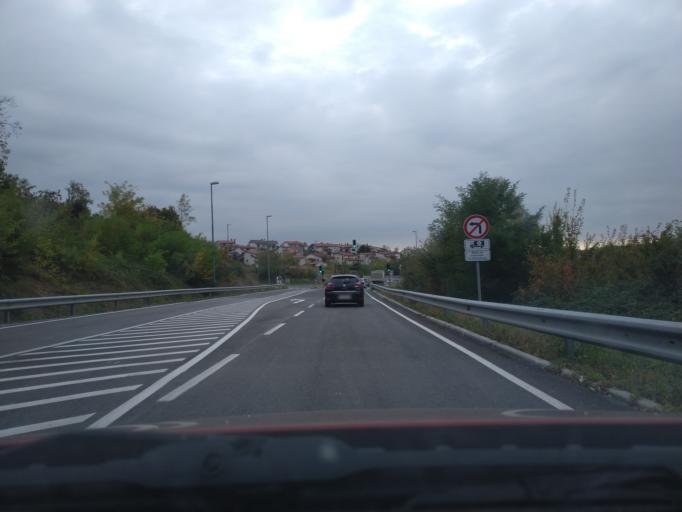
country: SI
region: Nova Gorica
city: Solkan
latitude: 45.9635
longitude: 13.6547
